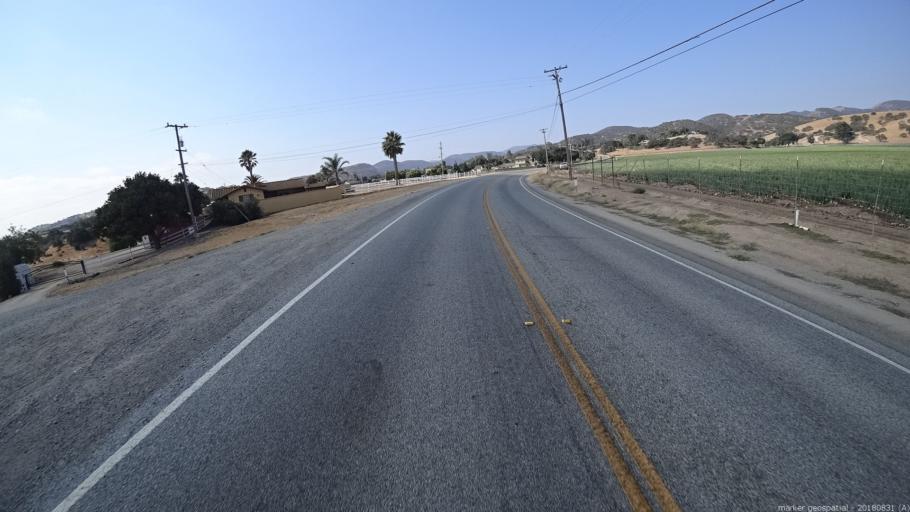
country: US
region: California
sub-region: Monterey County
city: King City
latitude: 36.1907
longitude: -121.1459
